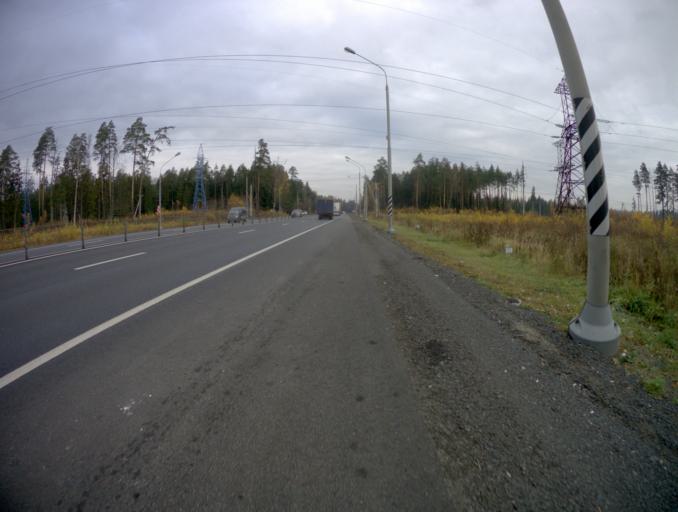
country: RU
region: Moskovskaya
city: Malaya Dubna
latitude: 55.8530
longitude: 38.9632
